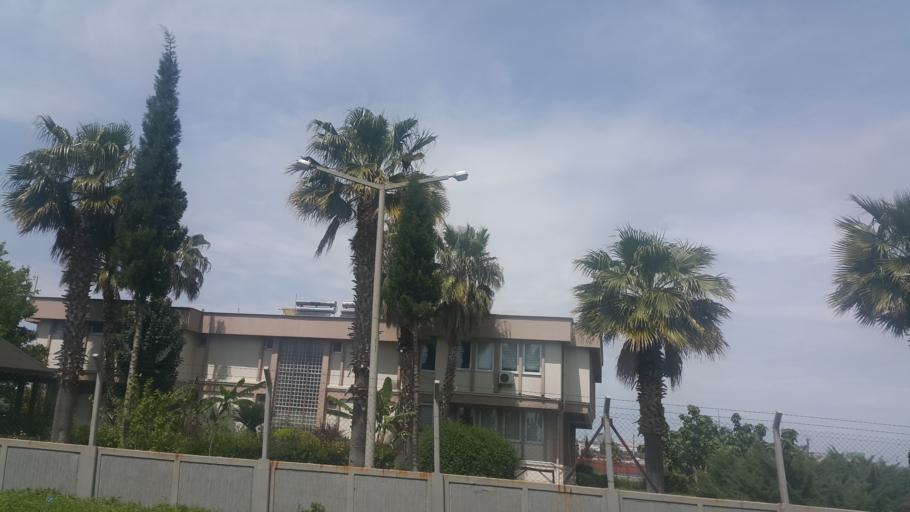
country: TR
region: Adana
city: Yakapinar
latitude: 36.9659
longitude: 35.6049
